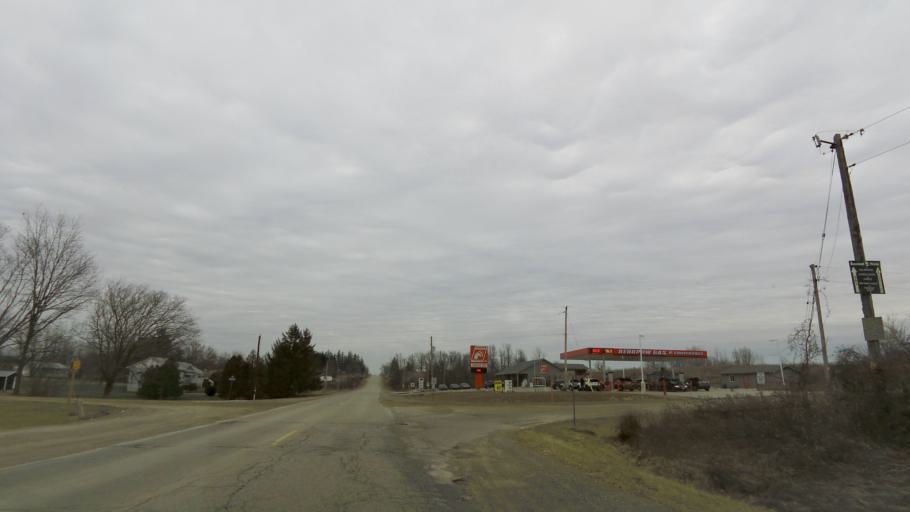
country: CA
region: Ontario
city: Brantford
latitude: 43.0654
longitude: -80.2214
